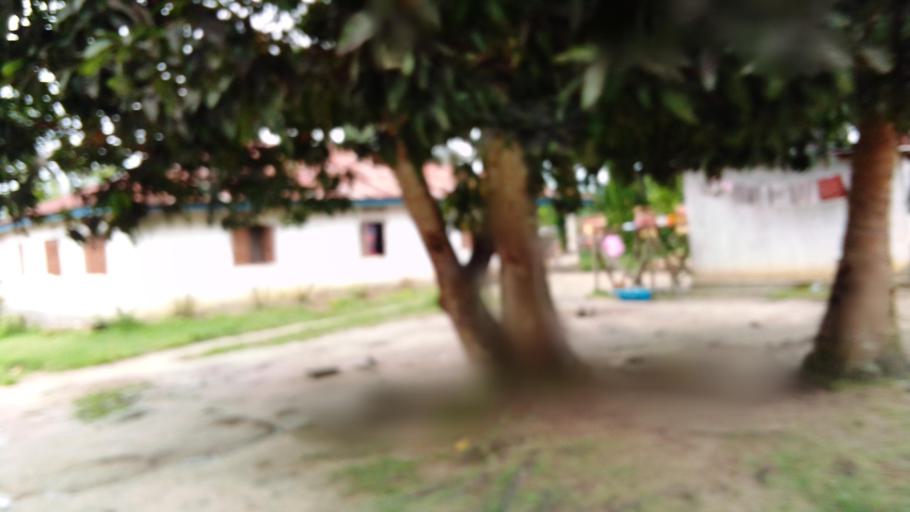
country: SL
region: Eastern Province
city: Kenema
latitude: 7.8553
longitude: -11.1880
